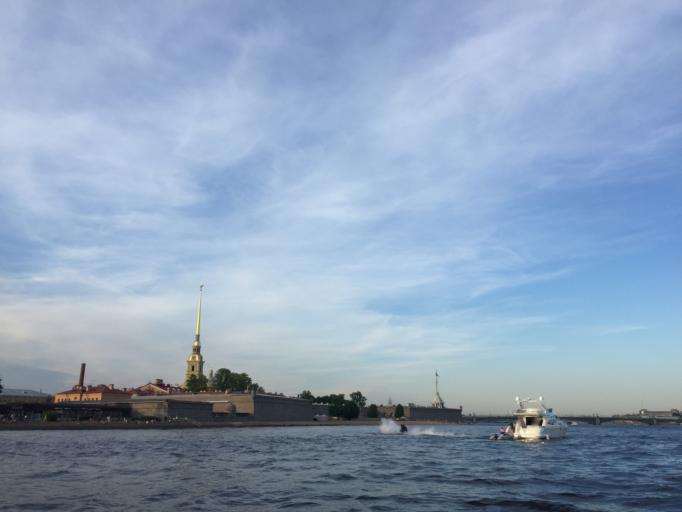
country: RU
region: St.-Petersburg
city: Saint Petersburg
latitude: 59.9466
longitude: 30.3094
